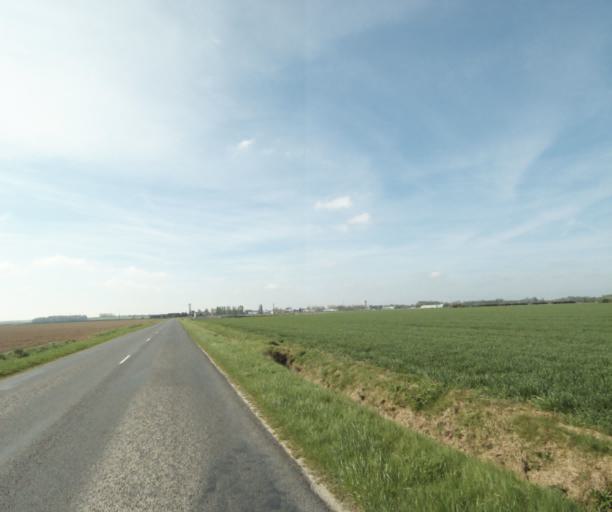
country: FR
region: Ile-de-France
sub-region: Departement de Seine-et-Marne
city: Nangis
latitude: 48.5703
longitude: 3.0392
